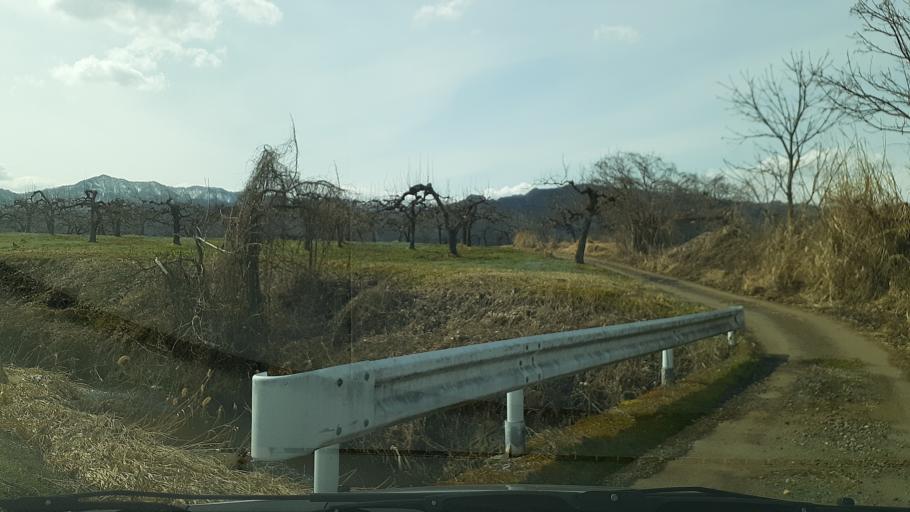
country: JP
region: Fukushima
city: Kitakata
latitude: 37.4562
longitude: 139.8238
